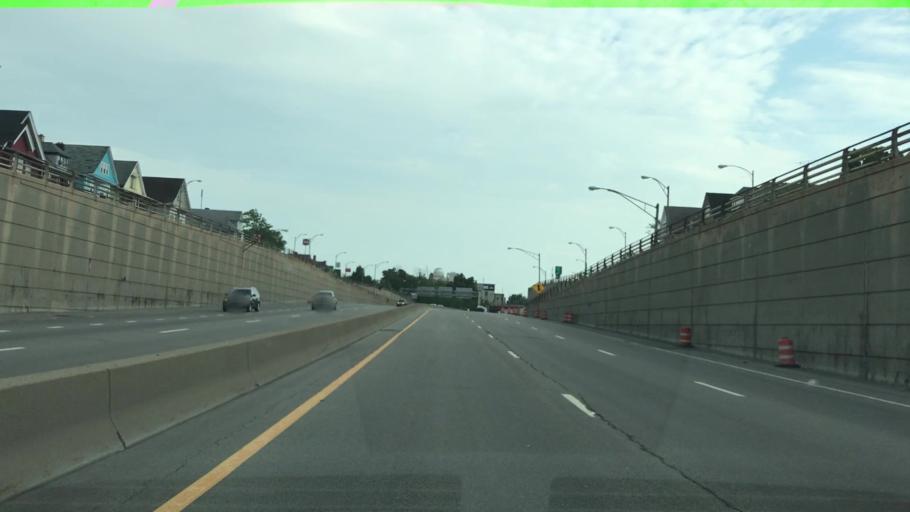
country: US
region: New York
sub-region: Erie County
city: Buffalo
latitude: 42.9106
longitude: -78.8434
